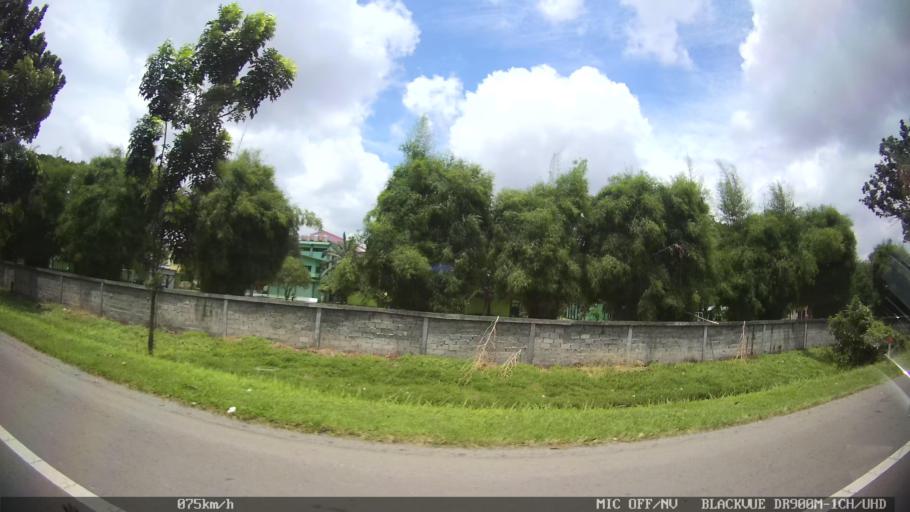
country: ID
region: North Sumatra
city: Medan
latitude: 3.6042
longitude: 98.7230
